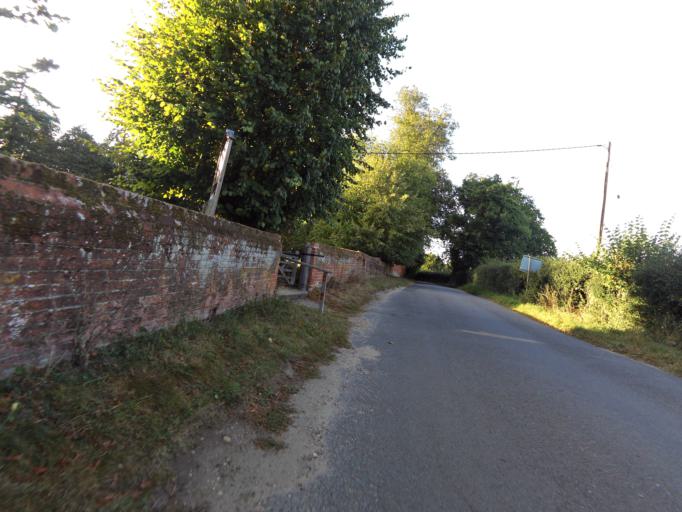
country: GB
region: England
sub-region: Suffolk
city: Kesgrave
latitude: 52.0114
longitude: 1.2297
